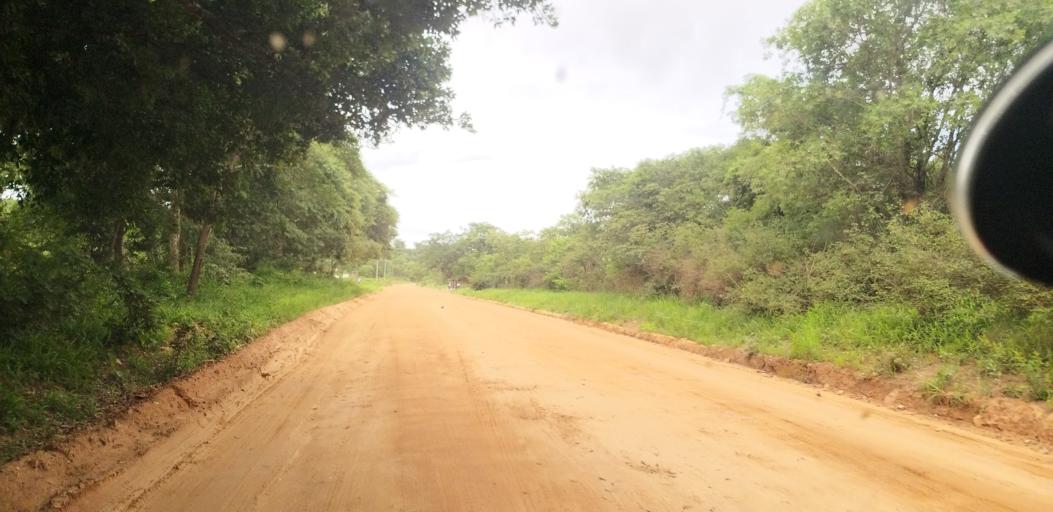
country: ZM
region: Lusaka
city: Lusaka
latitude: -15.1846
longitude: 28.4480
